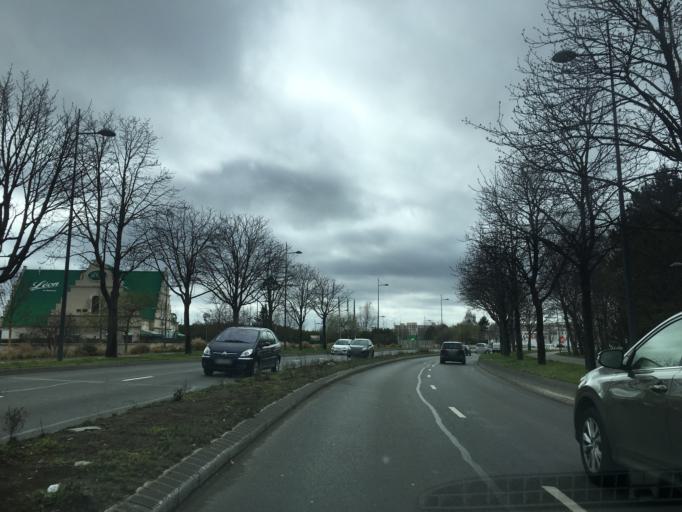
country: FR
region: Ile-de-France
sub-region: Departement du Val-de-Marne
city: Bonneuil-sur-Marne
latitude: 48.7702
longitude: 2.4897
